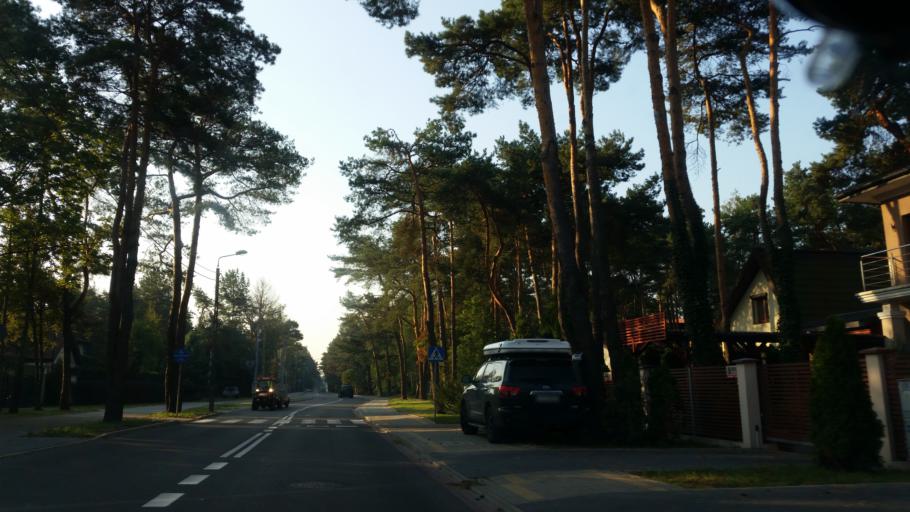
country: PL
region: Masovian Voivodeship
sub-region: Powiat otwocki
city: Jozefow
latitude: 52.1425
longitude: 21.2151
